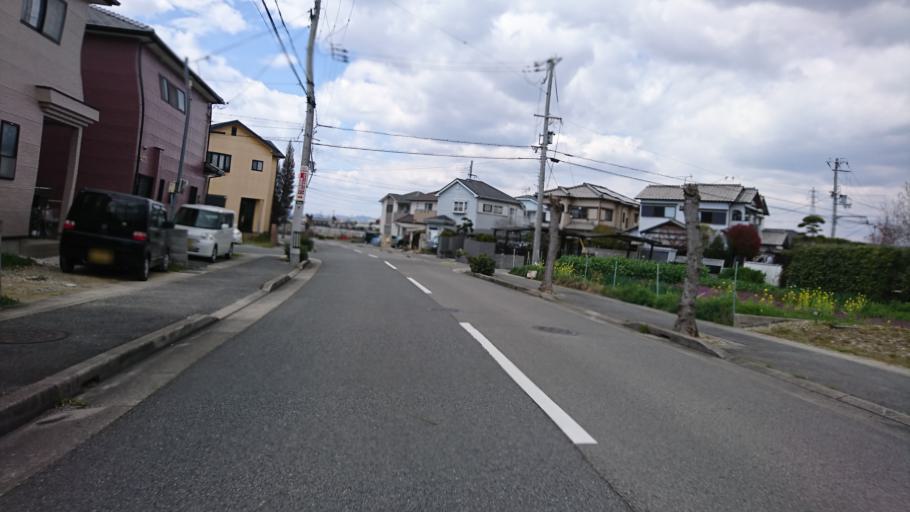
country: JP
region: Hyogo
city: Miki
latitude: 34.7511
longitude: 134.9160
